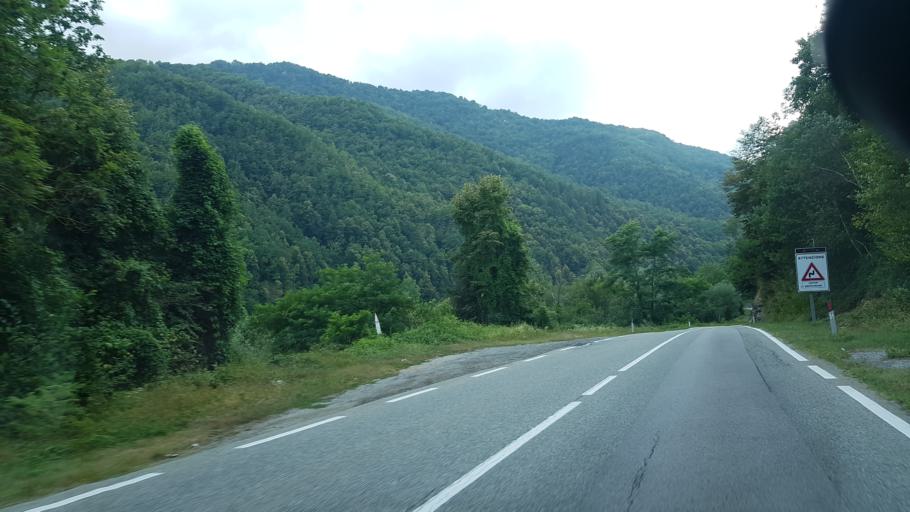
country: IT
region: Piedmont
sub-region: Provincia di Cuneo
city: Valmala
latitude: 44.5570
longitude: 7.3408
